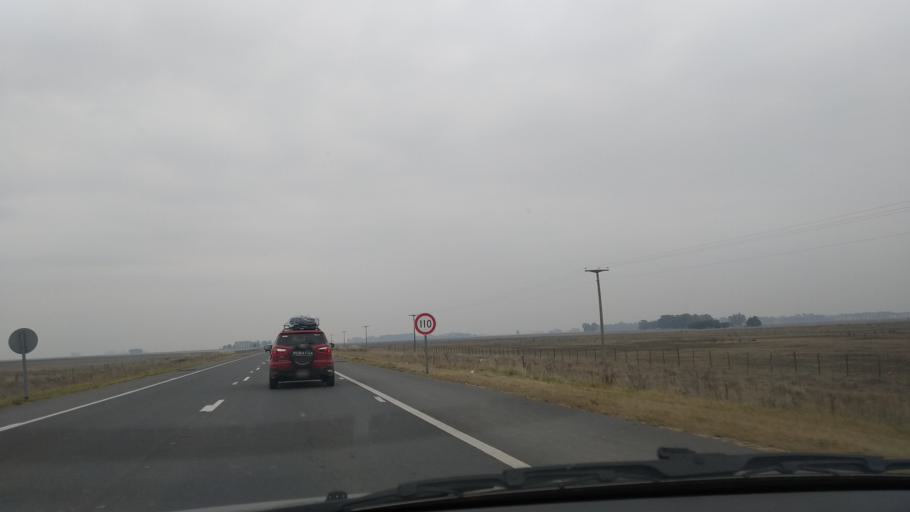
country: AR
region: Buenos Aires
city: Olavarria
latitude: -36.9913
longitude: -60.3174
